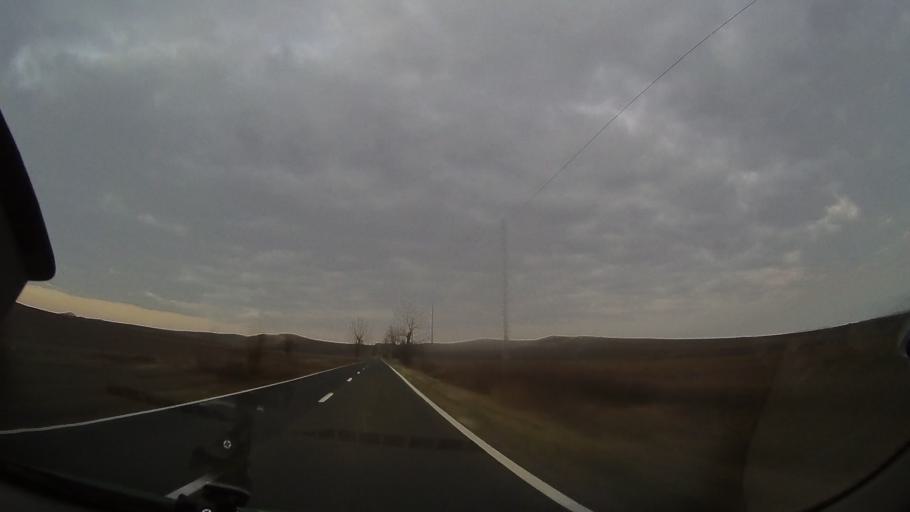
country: RO
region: Tulcea
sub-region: Comuna Nalbant
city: Nicolae Balcescu
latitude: 45.0069
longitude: 28.5979
